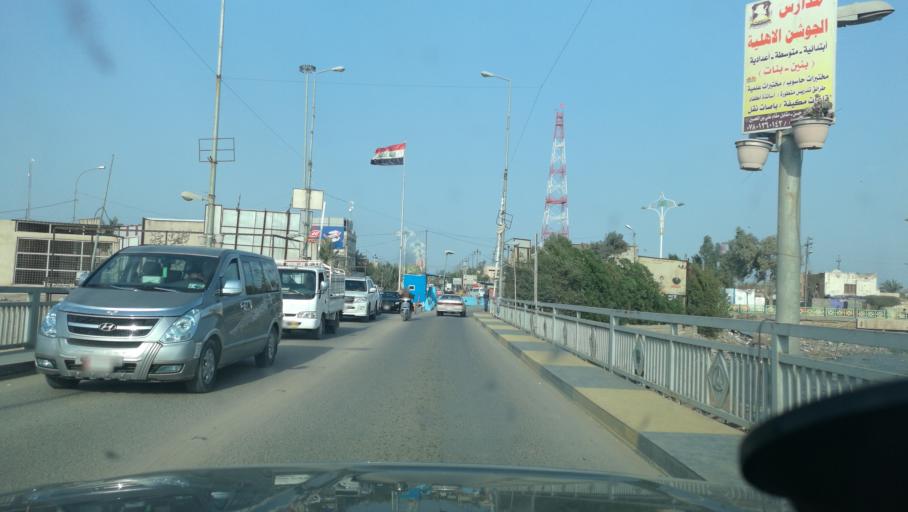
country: IQ
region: Basra Governorate
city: Al Basrah al Qadimah
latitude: 30.5237
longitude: 47.8453
